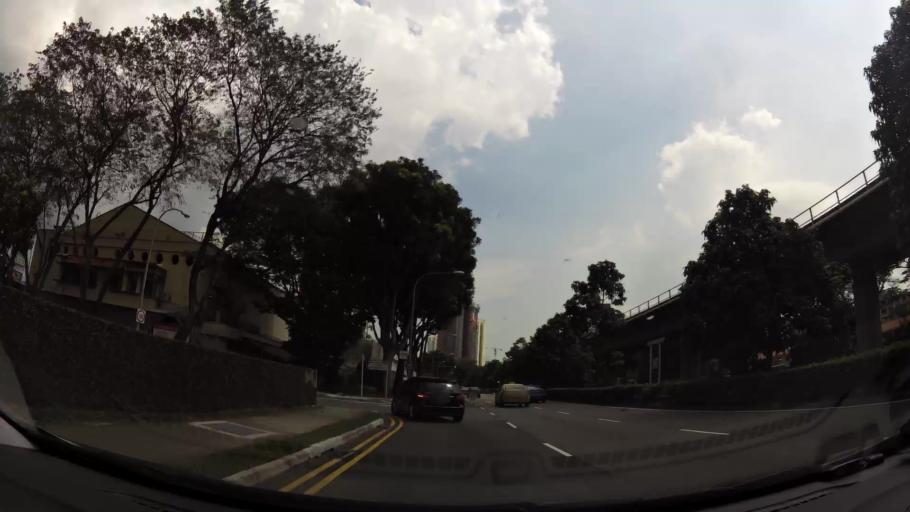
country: SG
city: Singapore
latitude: 1.2990
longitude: 103.8025
